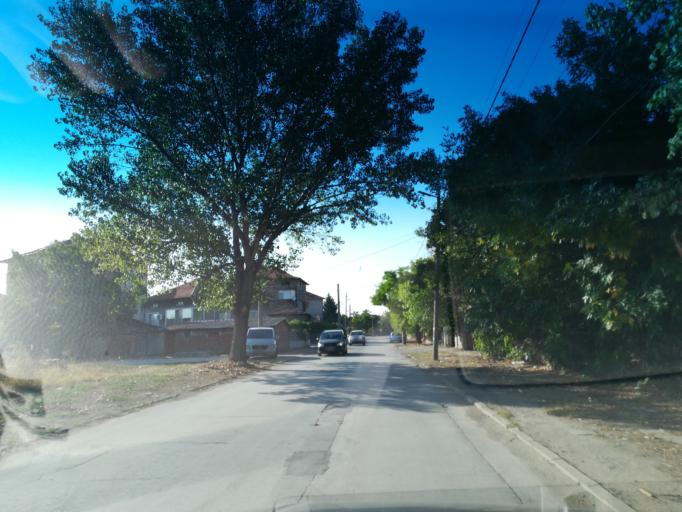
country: BG
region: Stara Zagora
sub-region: Obshtina Chirpan
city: Chirpan
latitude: 42.0944
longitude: 25.2340
